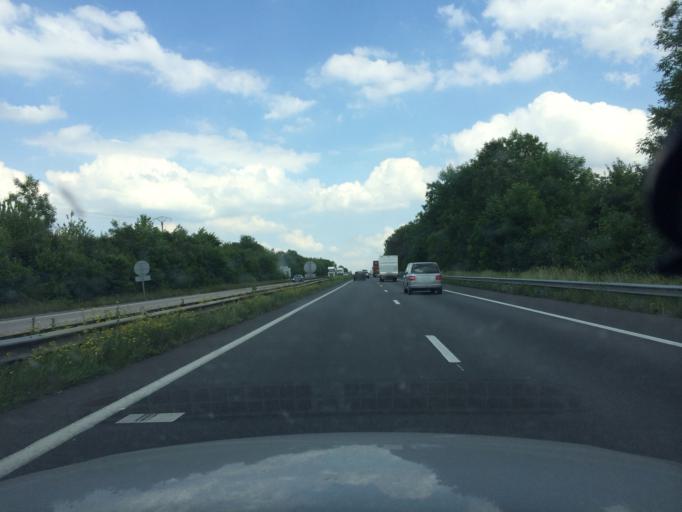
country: FR
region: Lorraine
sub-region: Departement de Meurthe-et-Moselle
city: Velaine-en-Haye
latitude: 48.6921
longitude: 6.0579
